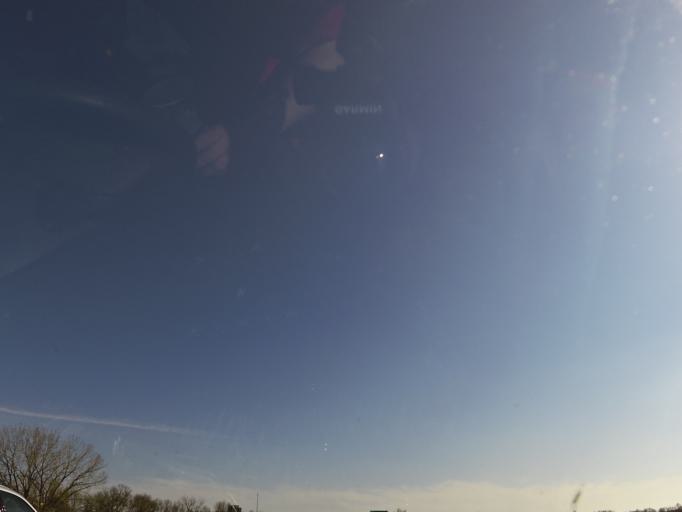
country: US
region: Minnesota
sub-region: Steele County
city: Owatonna
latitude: 44.0430
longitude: -93.2493
